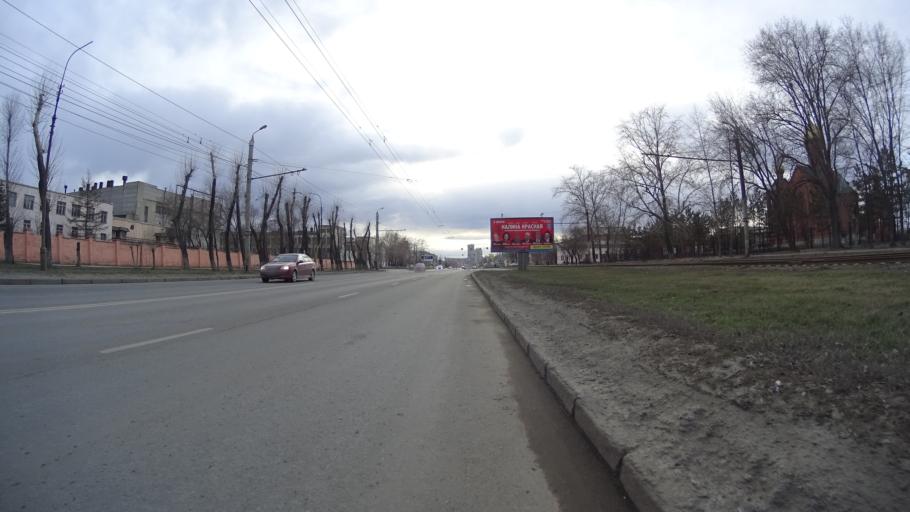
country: RU
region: Chelyabinsk
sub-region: Gorod Chelyabinsk
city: Chelyabinsk
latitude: 55.1599
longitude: 61.4559
